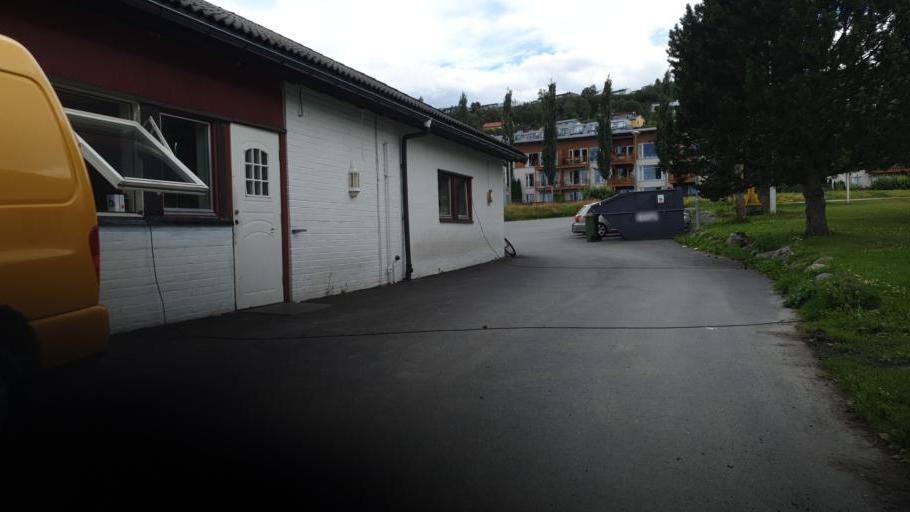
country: NO
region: Sor-Trondelag
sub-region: Malvik
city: Malvik
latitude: 63.4405
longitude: 10.6373
